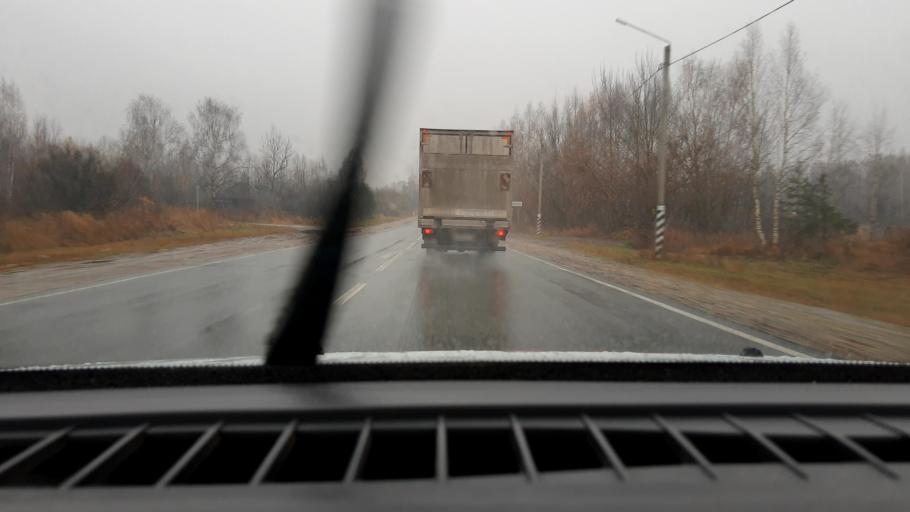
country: RU
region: Nizjnij Novgorod
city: Linda
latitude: 56.5715
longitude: 44.0239
